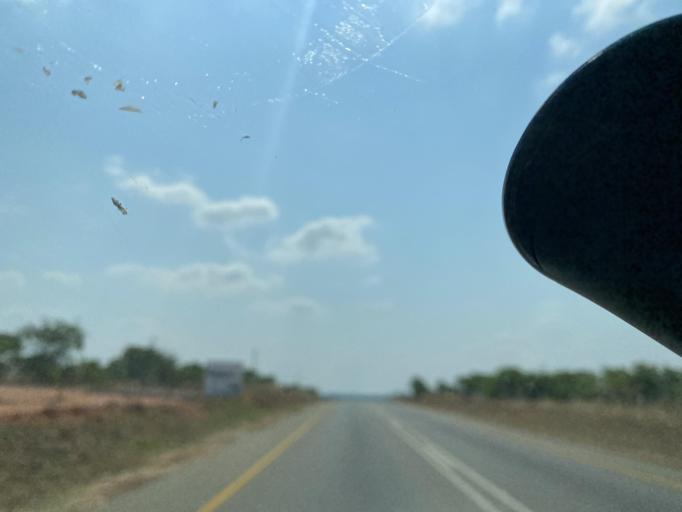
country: ZM
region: Lusaka
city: Chongwe
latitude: -15.5301
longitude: 28.6266
